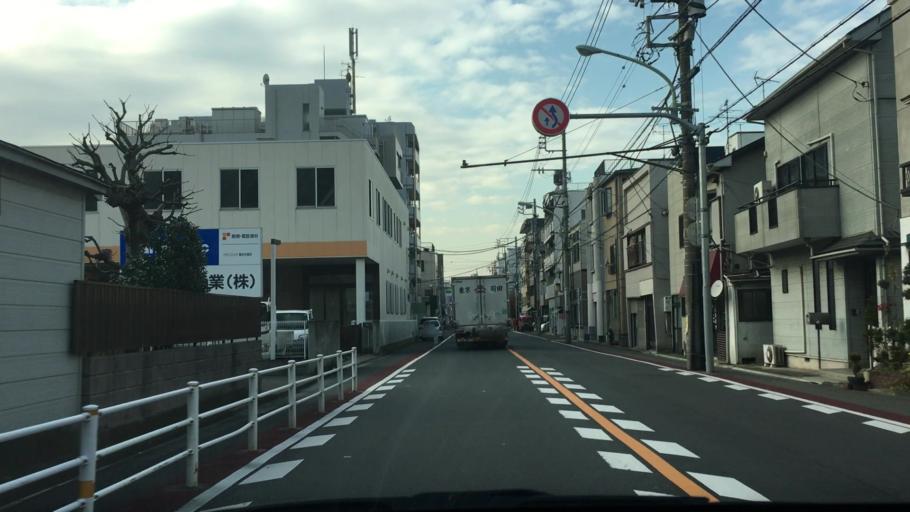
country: JP
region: Kanagawa
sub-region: Kawasaki-shi
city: Kawasaki
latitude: 35.5473
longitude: 139.7501
